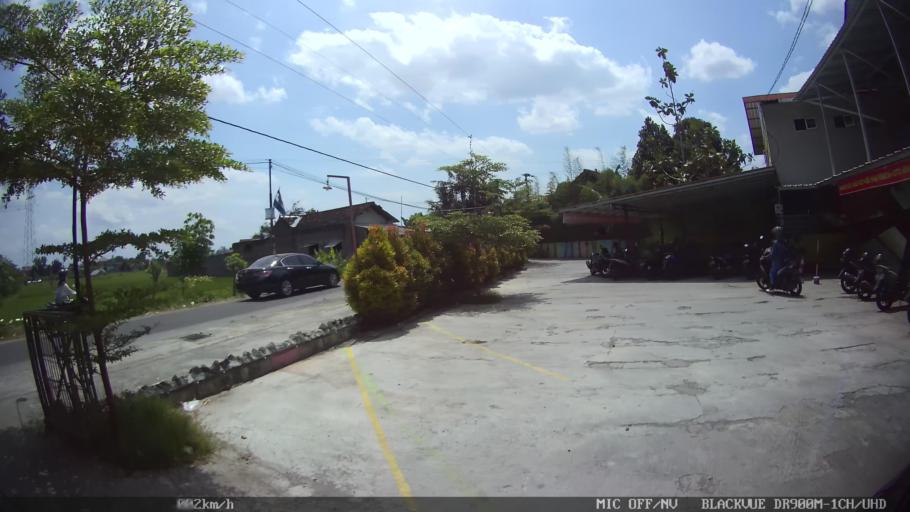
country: ID
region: Daerah Istimewa Yogyakarta
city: Kasihan
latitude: -7.8167
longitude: 110.3432
